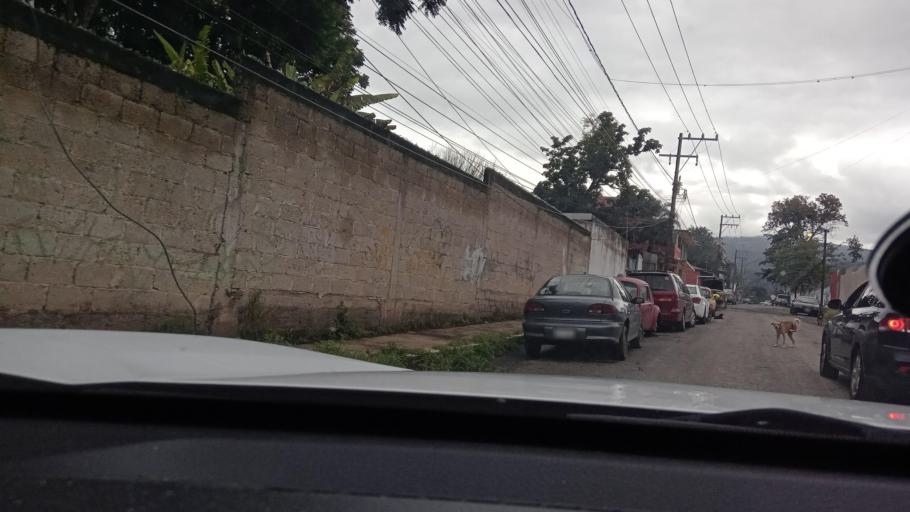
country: MX
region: Veracruz
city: Coatepec
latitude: 19.4484
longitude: -96.9705
